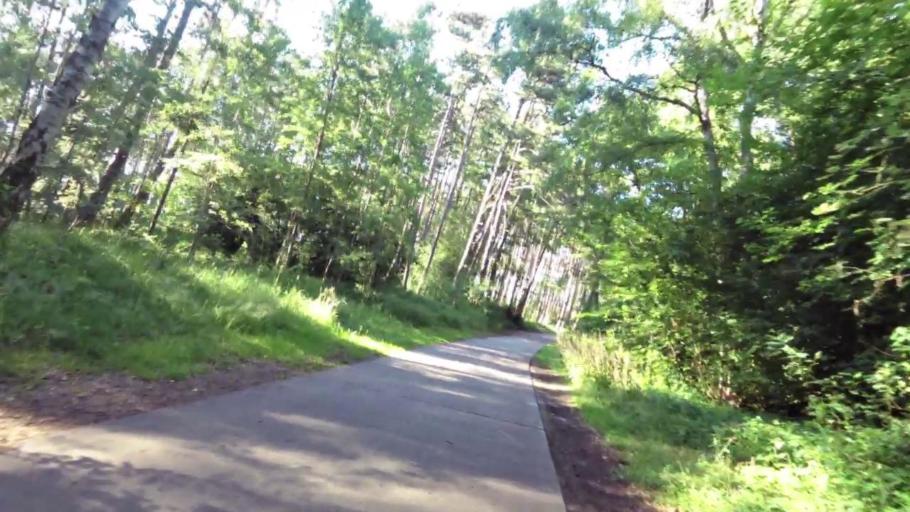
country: PL
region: West Pomeranian Voivodeship
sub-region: Powiat koszalinski
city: Sianow
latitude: 54.3546
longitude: 16.2740
